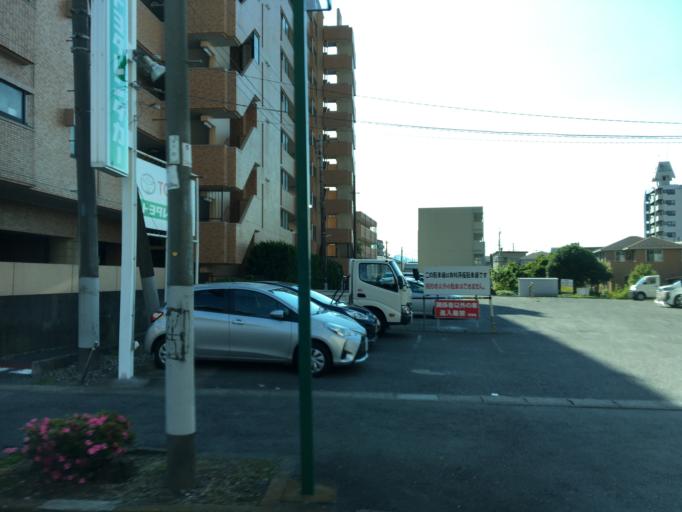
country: JP
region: Saitama
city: Sakado
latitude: 35.9596
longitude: 139.3941
